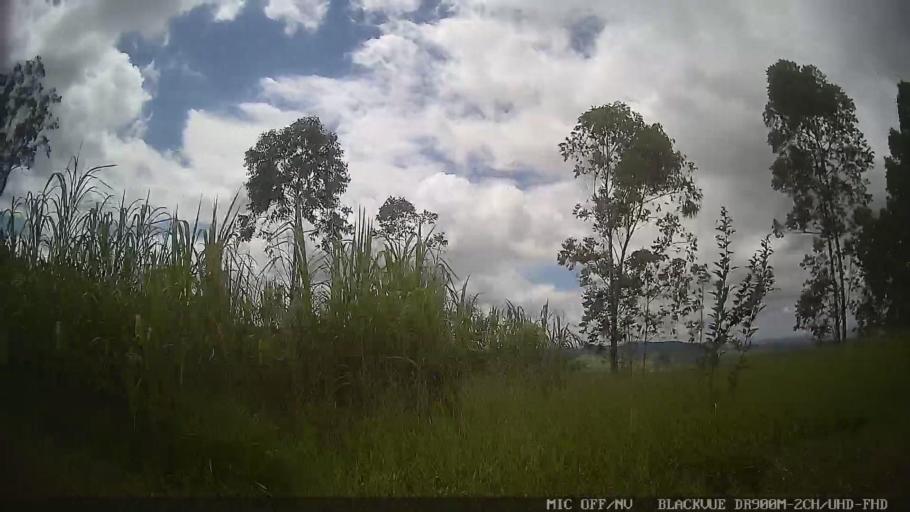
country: BR
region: Sao Paulo
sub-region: Braganca Paulista
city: Braganca Paulista
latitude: -22.8133
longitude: -46.5411
